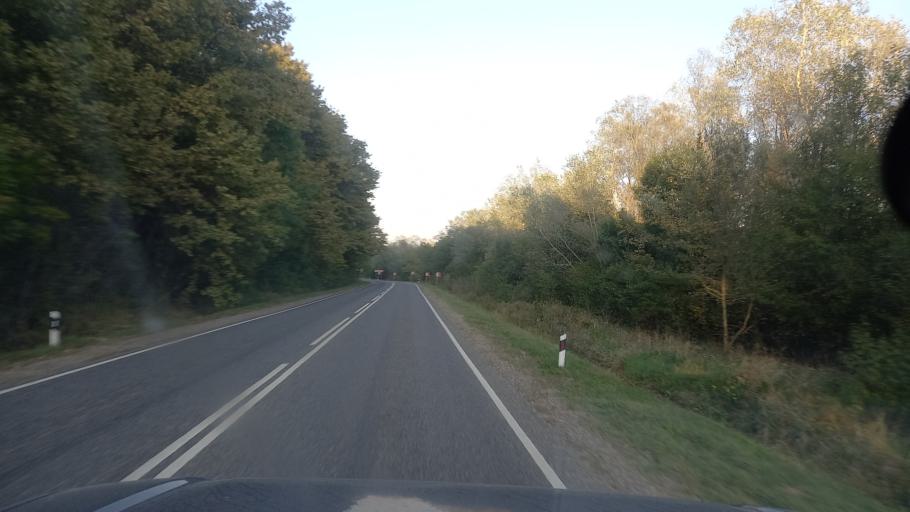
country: RU
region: Krasnodarskiy
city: Smolenskaya
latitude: 44.7491
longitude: 38.7599
